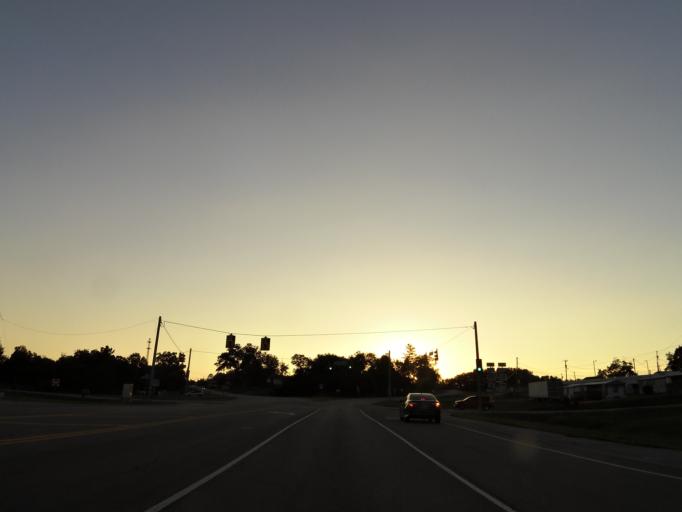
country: US
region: Tennessee
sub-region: Knox County
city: Mascot
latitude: 36.0260
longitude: -83.7290
